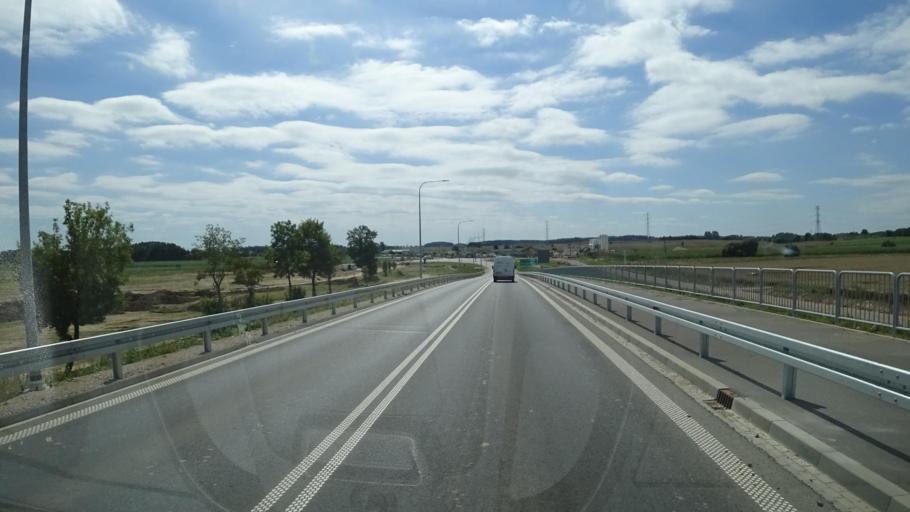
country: PL
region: Warmian-Masurian Voivodeship
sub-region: Powiat elcki
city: Elk
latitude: 53.7548
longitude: 22.3390
